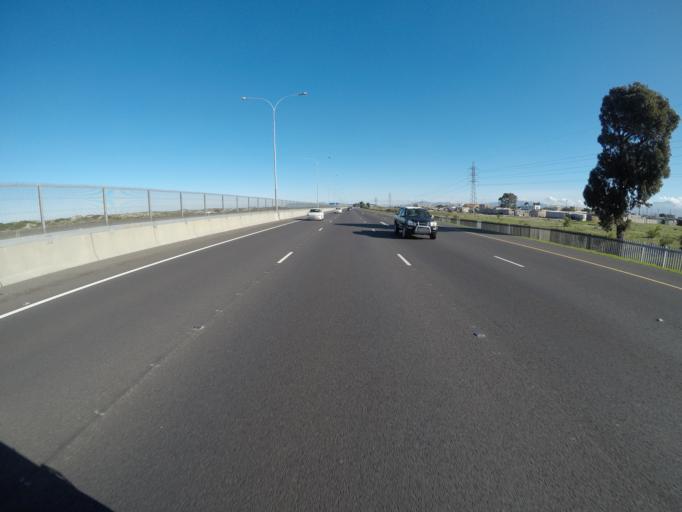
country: ZA
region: Western Cape
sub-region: City of Cape Town
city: Lansdowne
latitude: -33.9911
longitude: 18.6434
